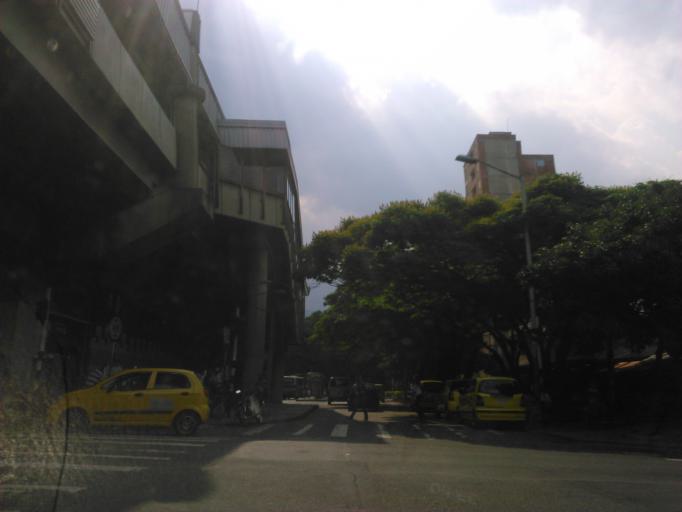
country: CO
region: Antioquia
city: Medellin
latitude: 6.2588
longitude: -75.5976
